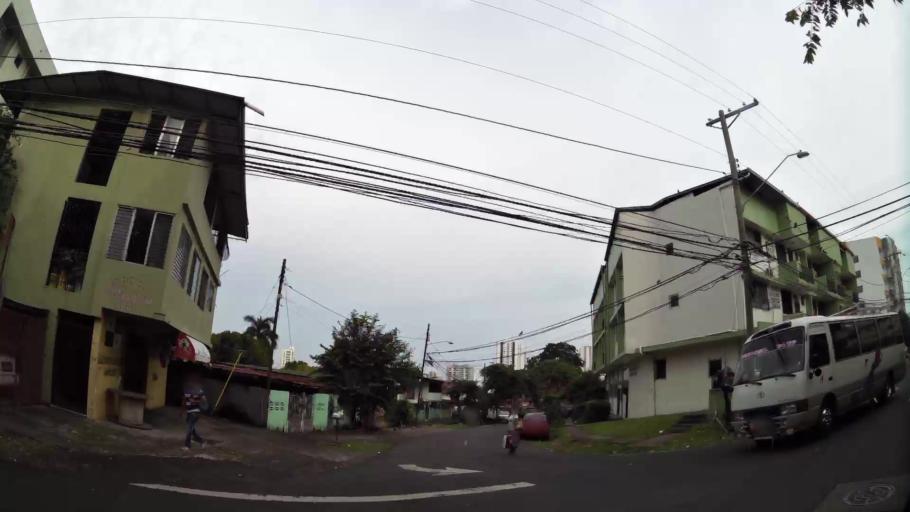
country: PA
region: Panama
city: Panama
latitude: 9.0070
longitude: -79.5055
